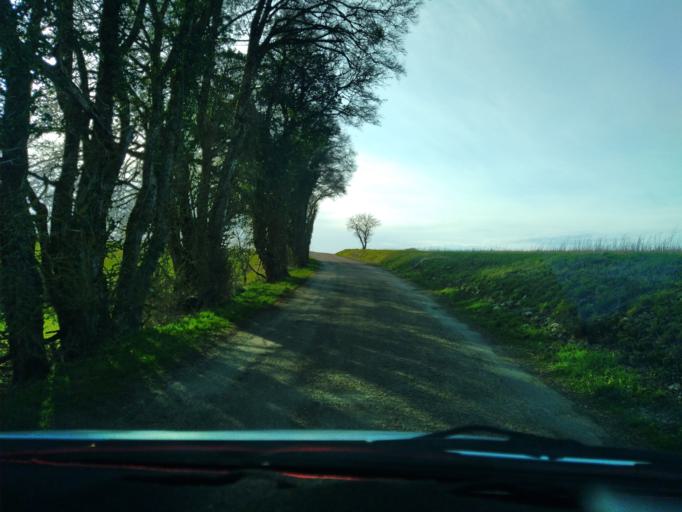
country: FR
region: Franche-Comte
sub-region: Departement de la Haute-Saone
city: Marnay
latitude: 47.3161
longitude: 5.6797
